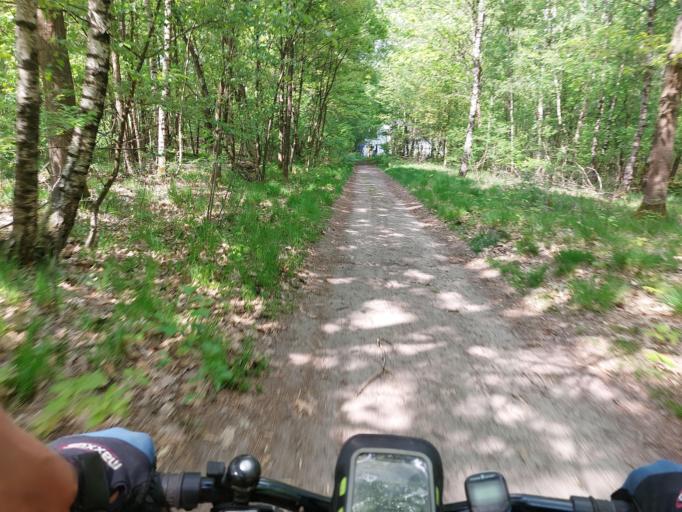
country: BE
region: Wallonia
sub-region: Province du Hainaut
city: Jurbise
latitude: 50.5023
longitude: 3.8786
